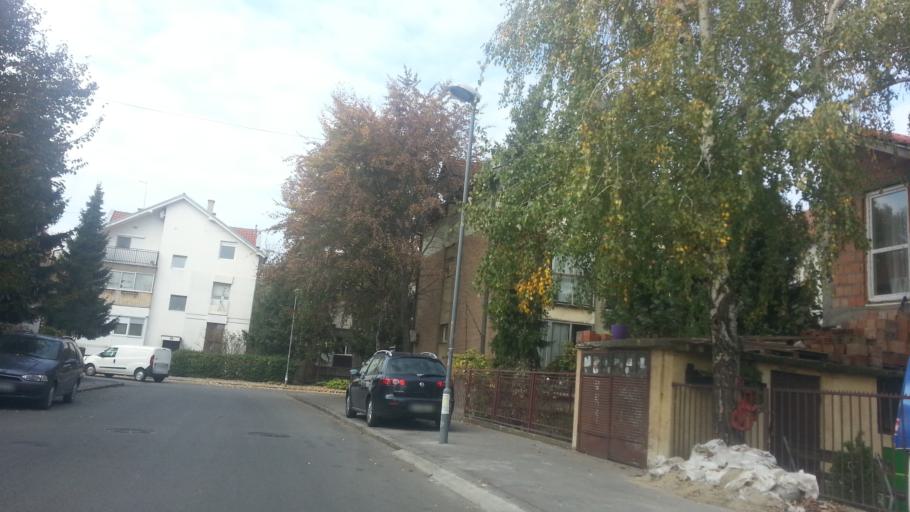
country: RS
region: Central Serbia
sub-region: Belgrade
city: Zemun
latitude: 44.8582
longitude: 20.3698
